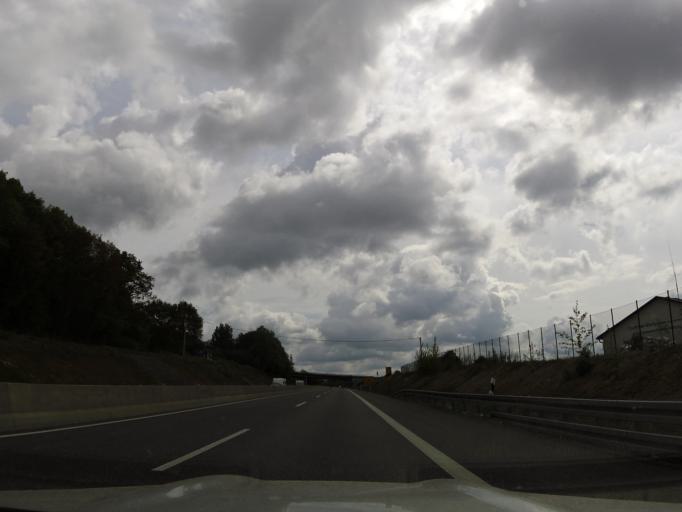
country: DE
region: Hesse
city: Merenberg
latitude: 50.4997
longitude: 8.2065
